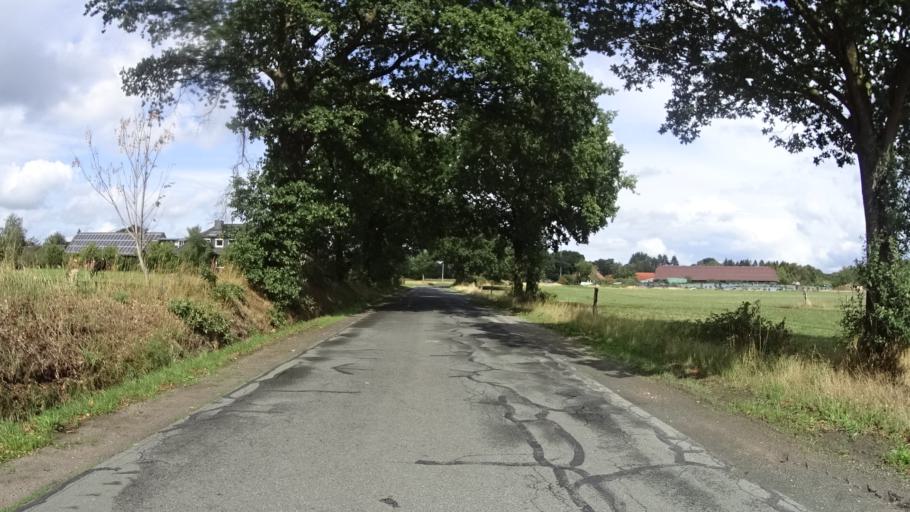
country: DE
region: Lower Saxony
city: Zetel
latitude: 53.3915
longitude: 7.9249
